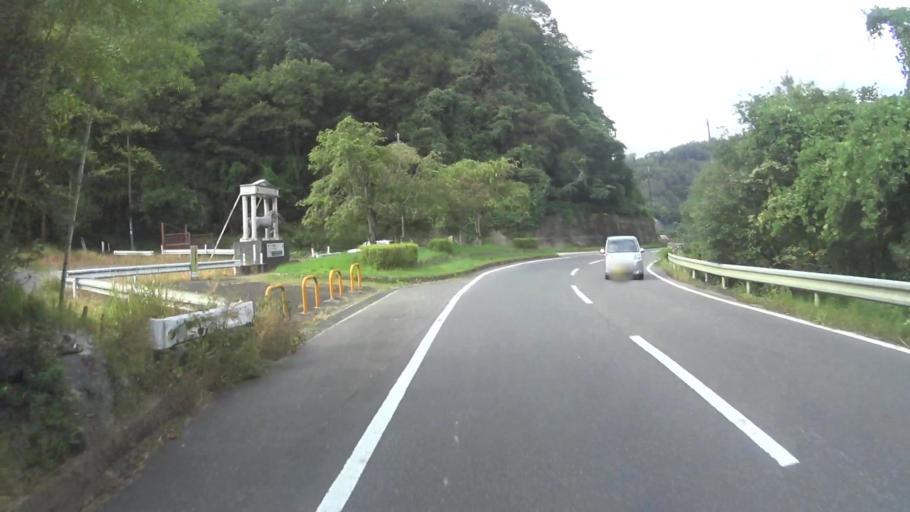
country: JP
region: Kyoto
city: Uji
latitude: 34.9111
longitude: 135.8709
